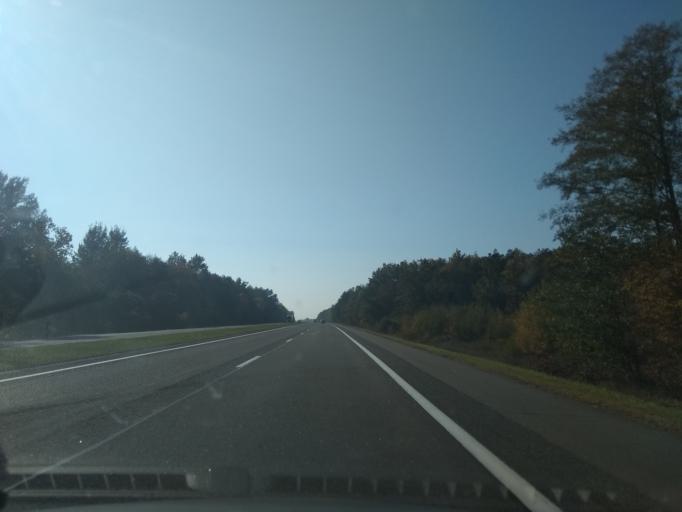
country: BY
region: Brest
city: Antopal'
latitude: 52.3432
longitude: 24.6567
